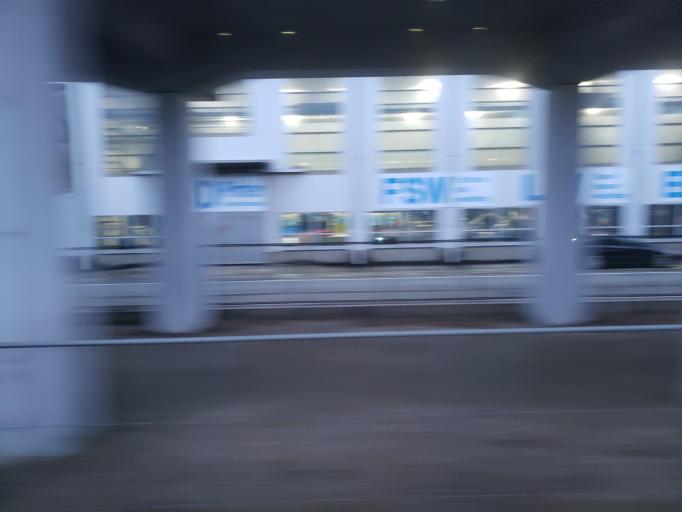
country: JP
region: Hyogo
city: Shirahamacho-usazakiminami
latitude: 34.8136
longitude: 134.7404
